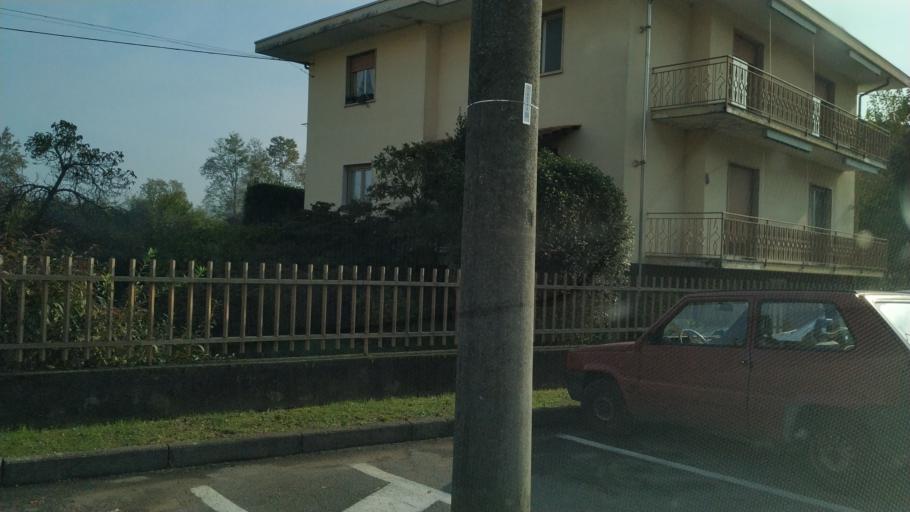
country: IT
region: Piedmont
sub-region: Provincia di Biella
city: Ceresane-Curanuova
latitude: 45.5202
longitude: 8.0075
